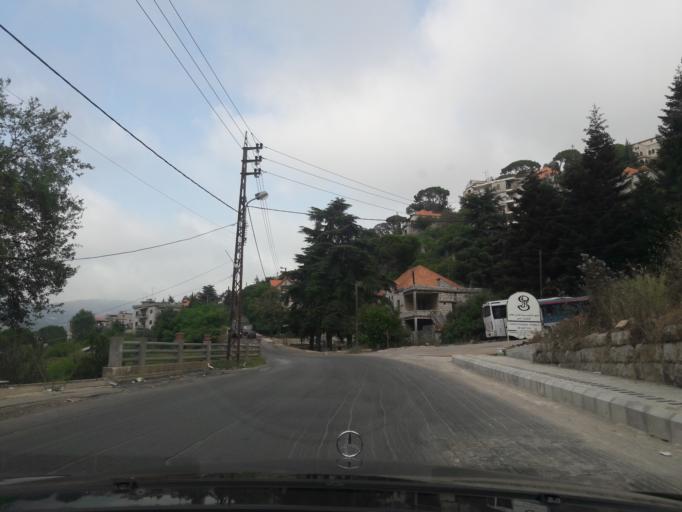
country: LB
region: Mont-Liban
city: Djounie
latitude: 33.9240
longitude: 35.7340
